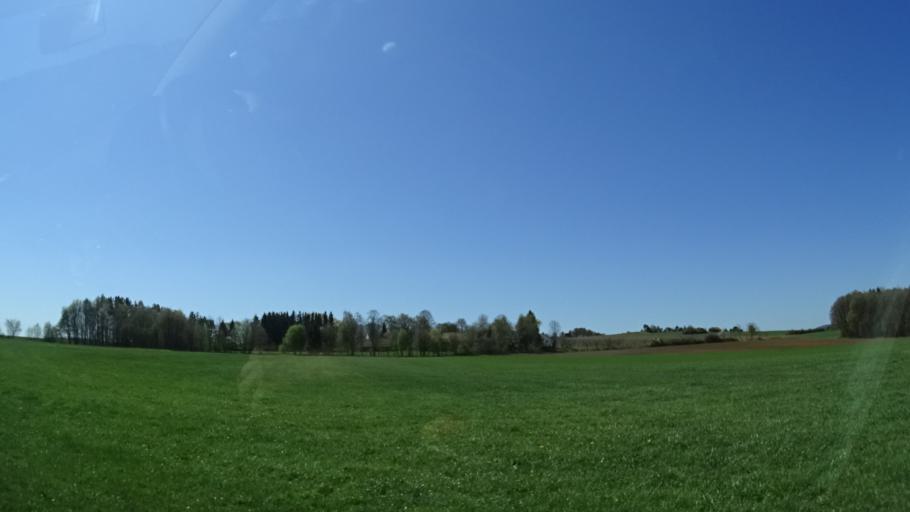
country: DE
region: Bavaria
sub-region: Upper Palatinate
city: Kastl
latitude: 49.3820
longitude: 11.6972
